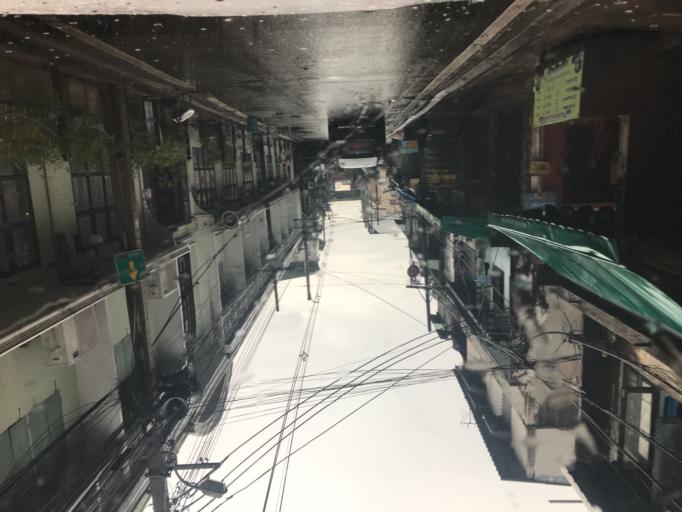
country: TH
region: Bangkok
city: Bangkok Noi
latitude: 13.7512
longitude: 100.4713
